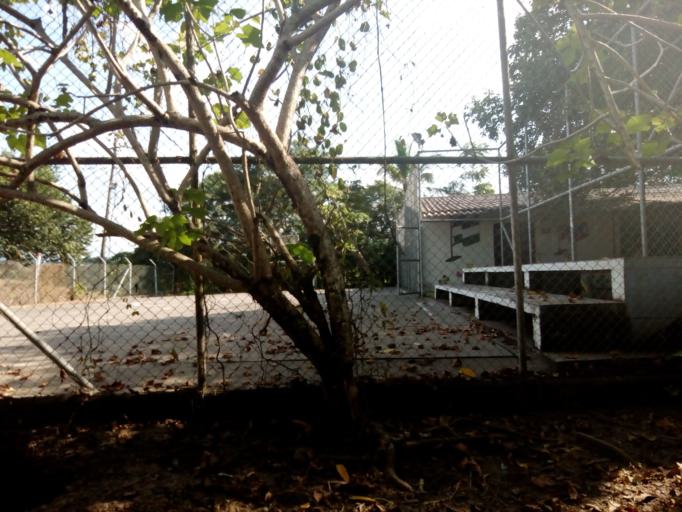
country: CO
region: Boyaca
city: Puerto Boyaca
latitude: 5.9013
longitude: -74.4042
